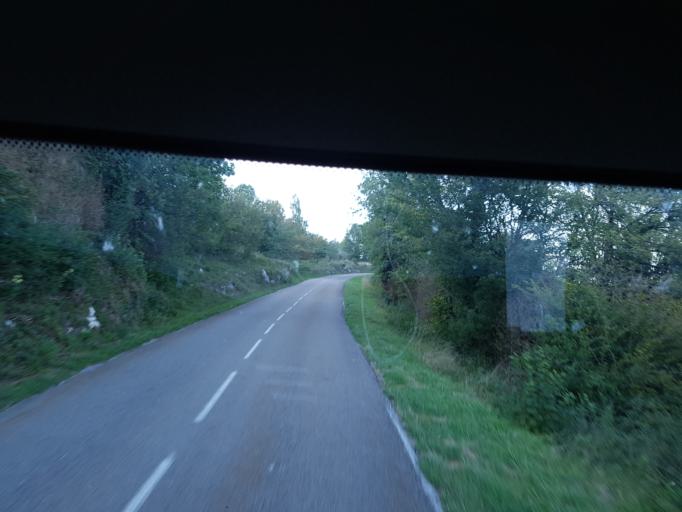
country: FR
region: Franche-Comte
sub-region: Departement du Jura
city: Moirans-en-Montagne
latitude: 46.4164
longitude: 5.6490
